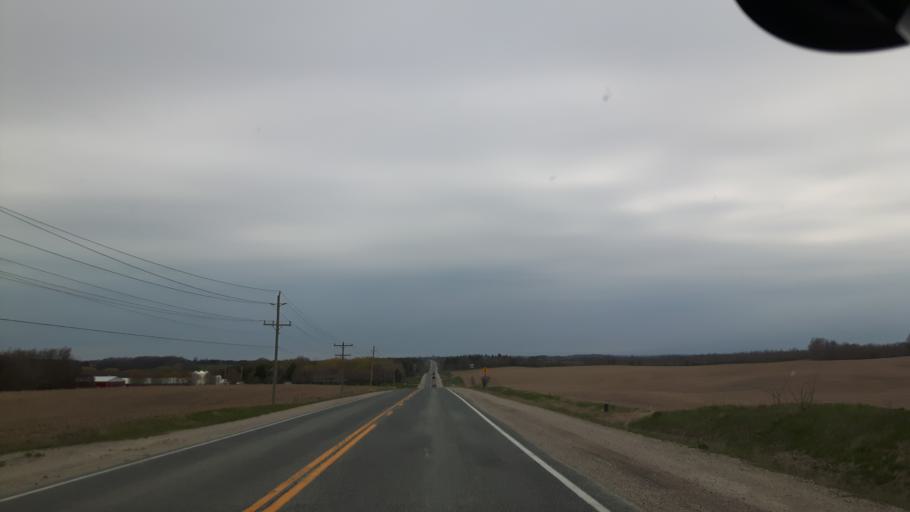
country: CA
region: Ontario
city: Goderich
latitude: 43.6589
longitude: -81.6172
